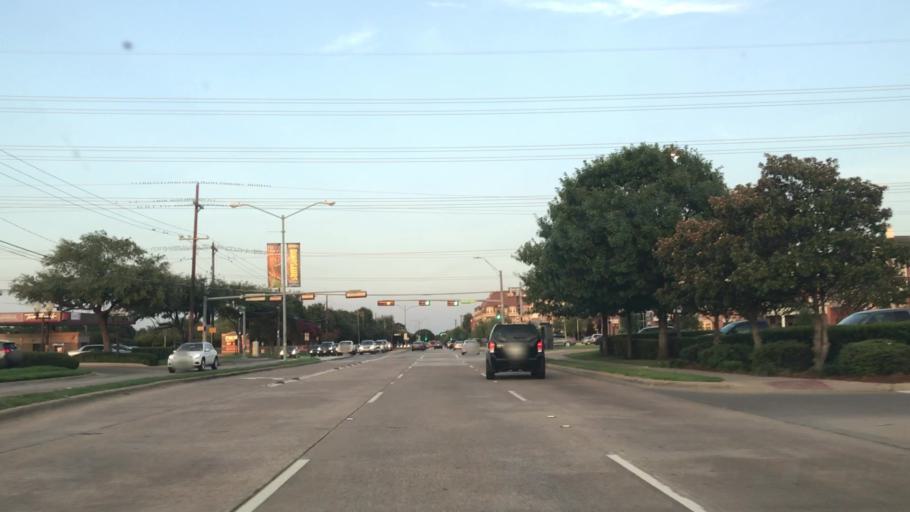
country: US
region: Texas
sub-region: Dallas County
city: Highland Park
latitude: 32.8510
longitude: -96.7687
